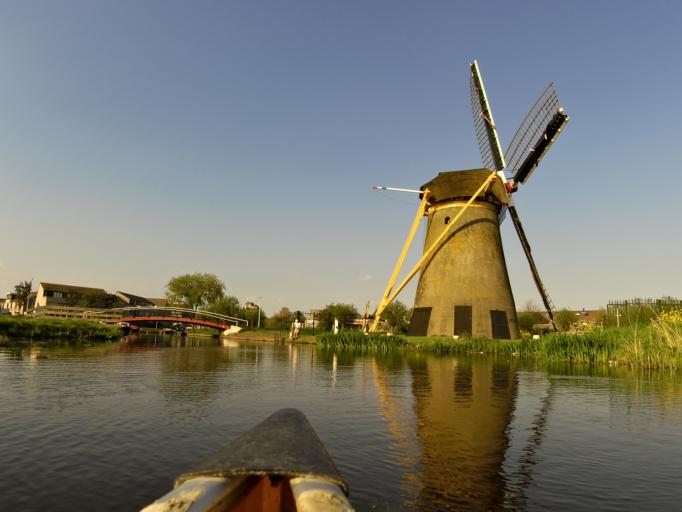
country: NL
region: South Holland
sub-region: Gemeente Voorschoten
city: Voorschoten
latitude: 52.1506
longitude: 4.4427
